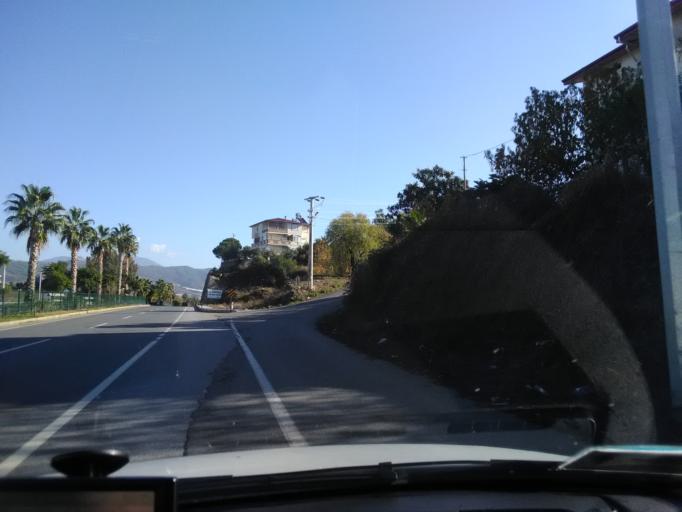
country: TR
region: Antalya
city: Gazipasa
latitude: 36.2561
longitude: 32.3289
